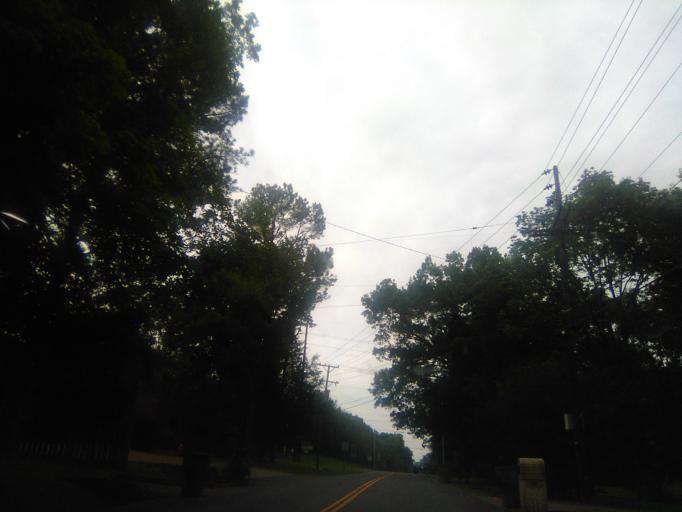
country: US
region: Tennessee
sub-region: Davidson County
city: Belle Meade
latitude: 36.1184
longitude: -86.8873
